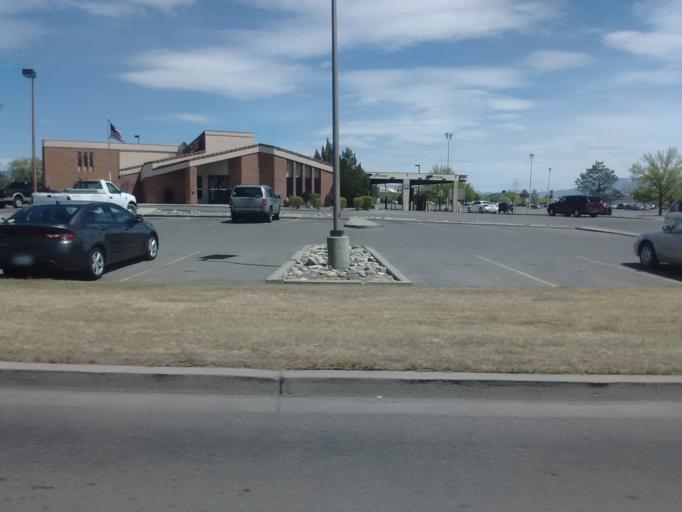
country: US
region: Colorado
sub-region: Mesa County
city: Redlands
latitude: 39.0940
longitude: -108.6056
